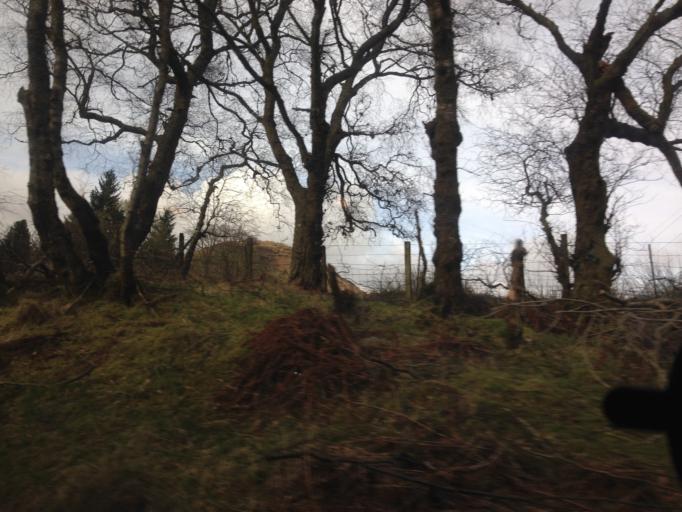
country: GB
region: Scotland
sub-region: Argyll and Bute
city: Garelochhead
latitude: 56.1622
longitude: -4.7798
